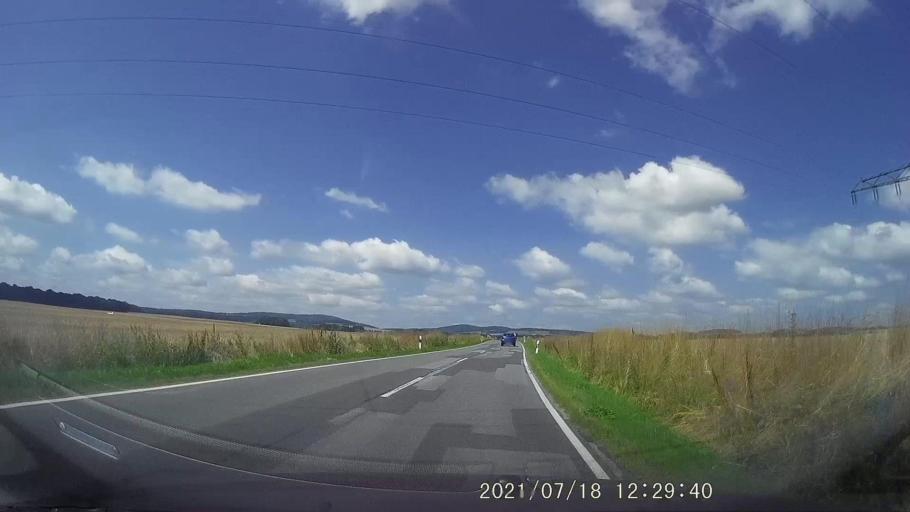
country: DE
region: Saxony
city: Markersdorf
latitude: 51.1676
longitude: 14.9194
